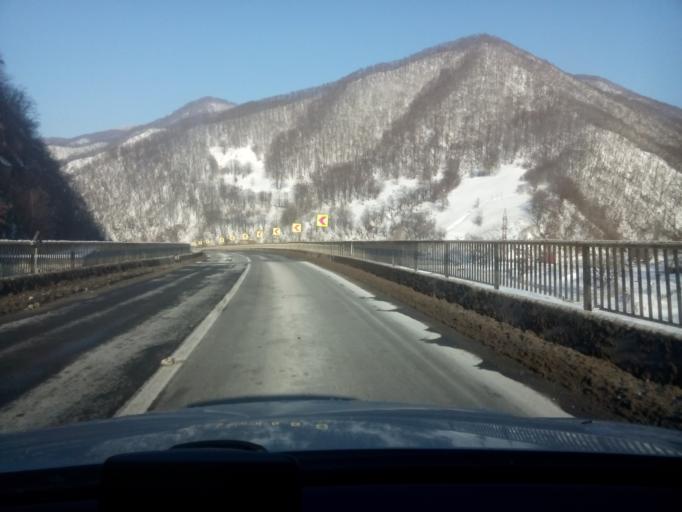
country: RO
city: Cainenii Mici
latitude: 45.5323
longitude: 24.2705
